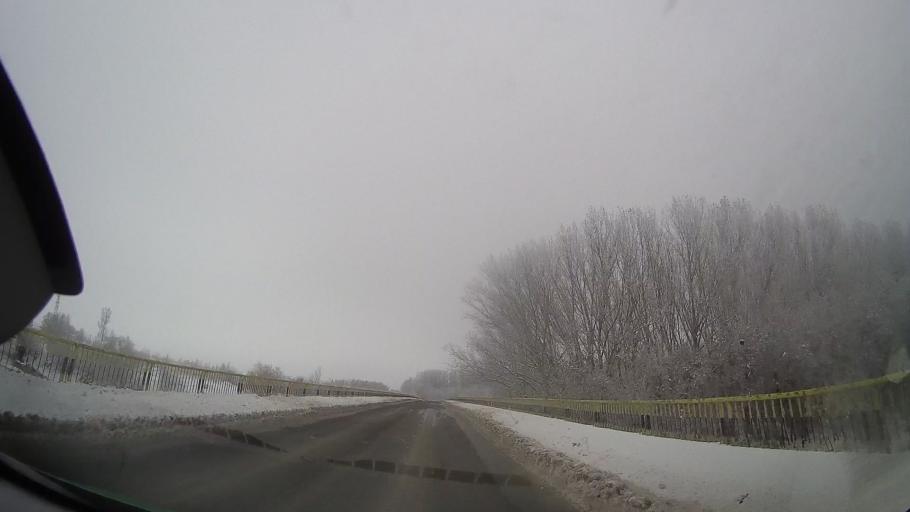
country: RO
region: Neamt
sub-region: Comuna Horia
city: Cotu Vames
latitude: 46.8828
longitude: 26.9708
